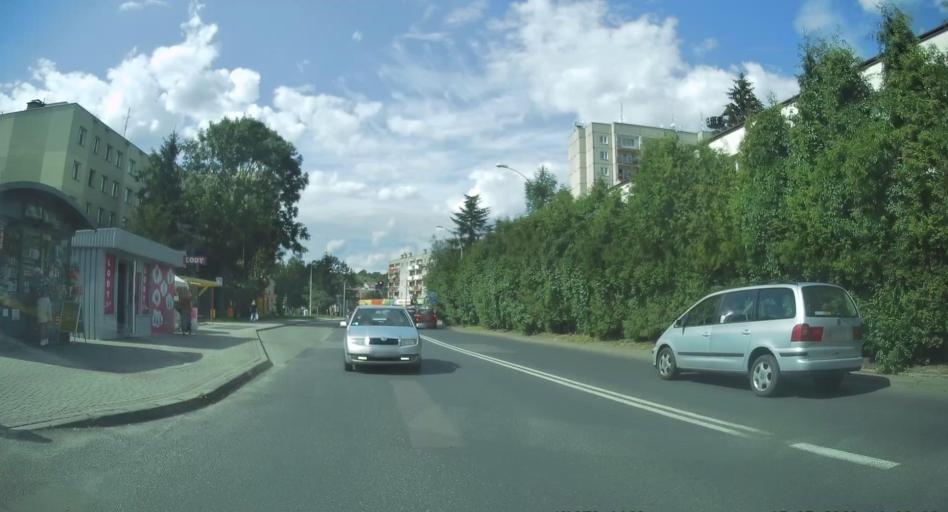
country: PL
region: Subcarpathian Voivodeship
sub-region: Przemysl
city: Przemysl
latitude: 49.7908
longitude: 22.7729
